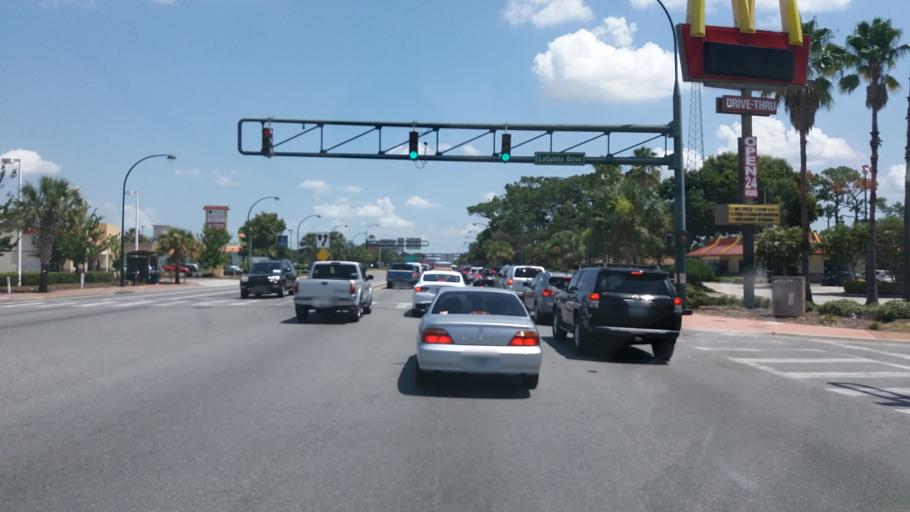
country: US
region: Florida
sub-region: Orange County
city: Sky Lake
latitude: 28.4407
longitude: -81.4035
